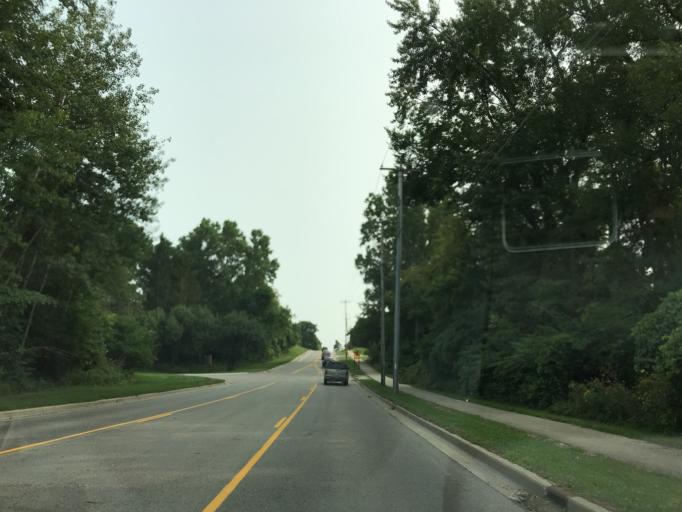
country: US
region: Michigan
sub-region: Ingham County
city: Okemos
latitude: 42.7458
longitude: -84.4475
